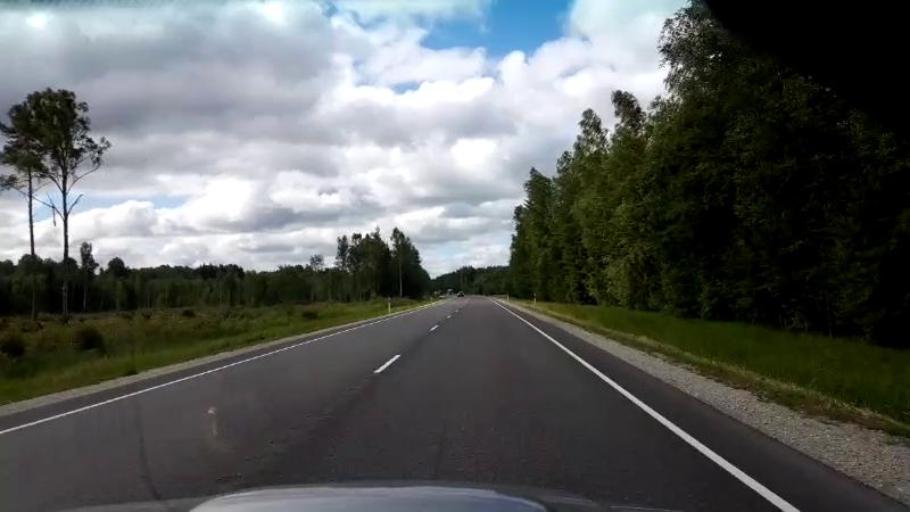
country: EE
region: Raplamaa
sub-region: Maerjamaa vald
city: Marjamaa
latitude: 58.8215
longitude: 24.4134
